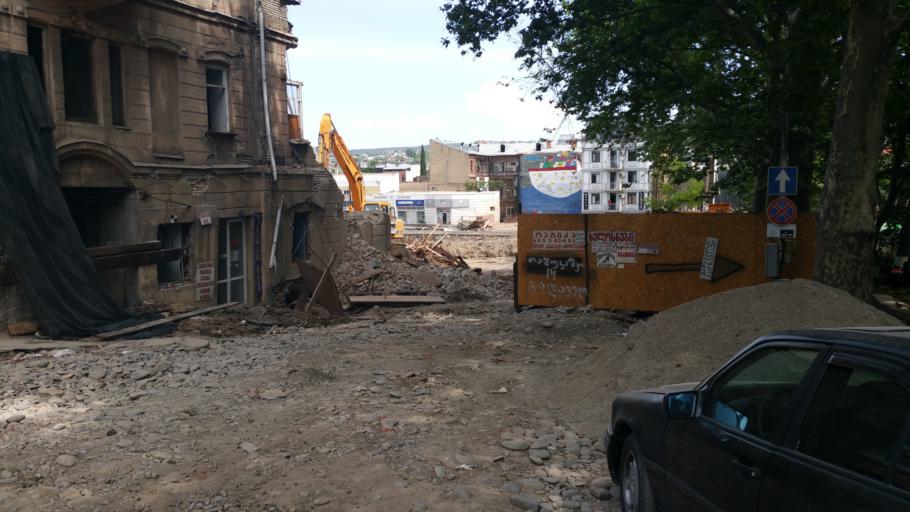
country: GE
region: T'bilisi
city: Tbilisi
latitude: 41.6976
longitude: 44.8017
